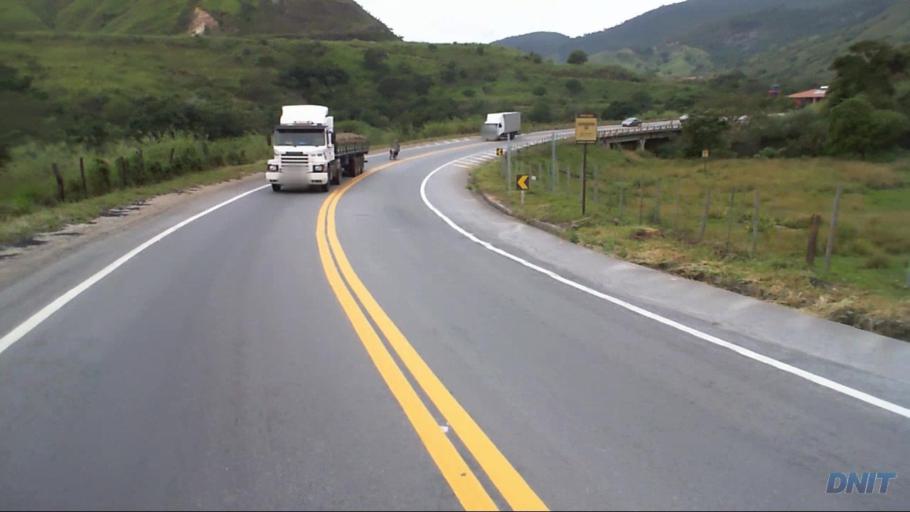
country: BR
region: Minas Gerais
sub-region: Timoteo
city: Timoteo
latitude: -19.6168
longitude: -42.7836
